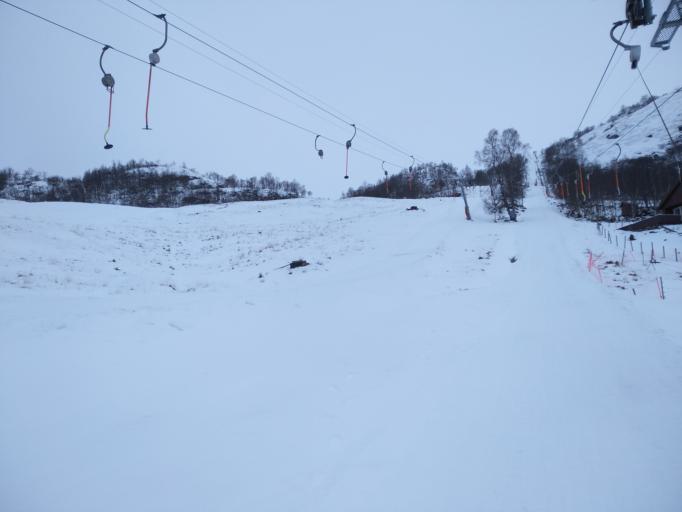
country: NO
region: Vest-Agder
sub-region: Sirdal
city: Tonstad
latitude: 59.0222
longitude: 6.9220
